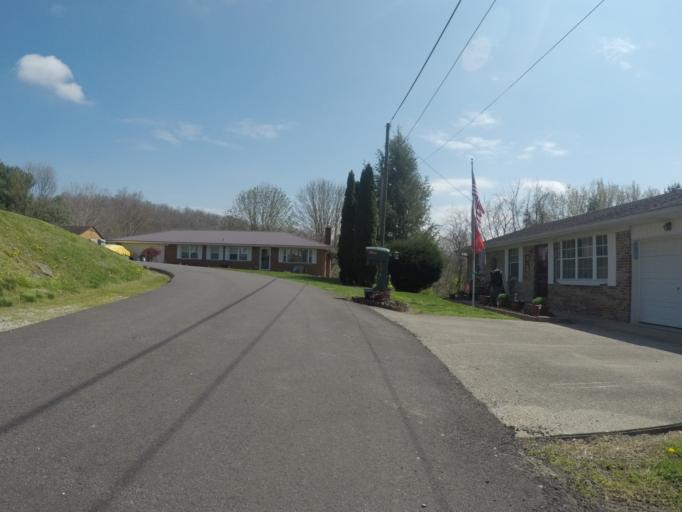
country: US
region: Ohio
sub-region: Lawrence County
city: Burlington
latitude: 38.3792
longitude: -82.5295
